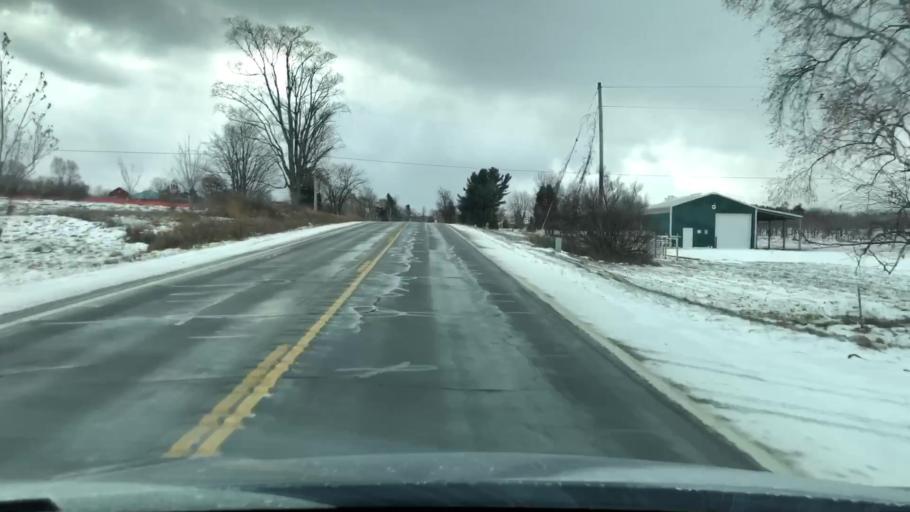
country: US
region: Michigan
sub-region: Antrim County
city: Elk Rapids
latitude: 44.8747
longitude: -85.5153
